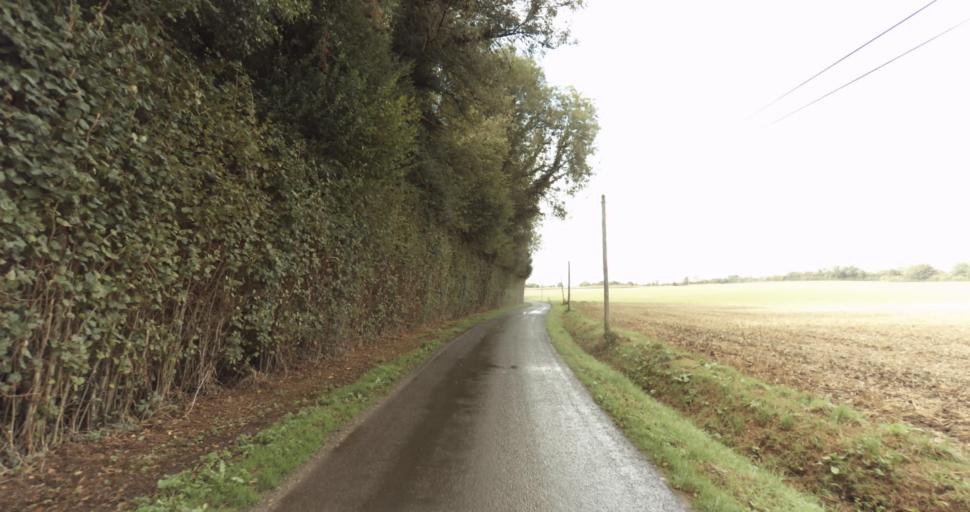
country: FR
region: Lower Normandy
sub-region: Departement de l'Orne
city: Sainte-Gauburge-Sainte-Colombe
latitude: 48.6929
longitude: 0.3808
